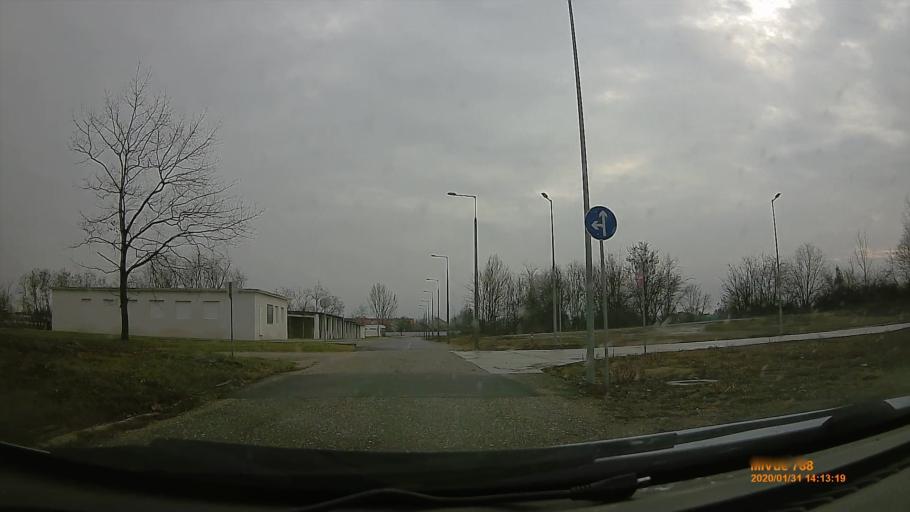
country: HU
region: Szabolcs-Szatmar-Bereg
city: Nyiregyhaza
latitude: 47.9553
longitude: 21.6806
